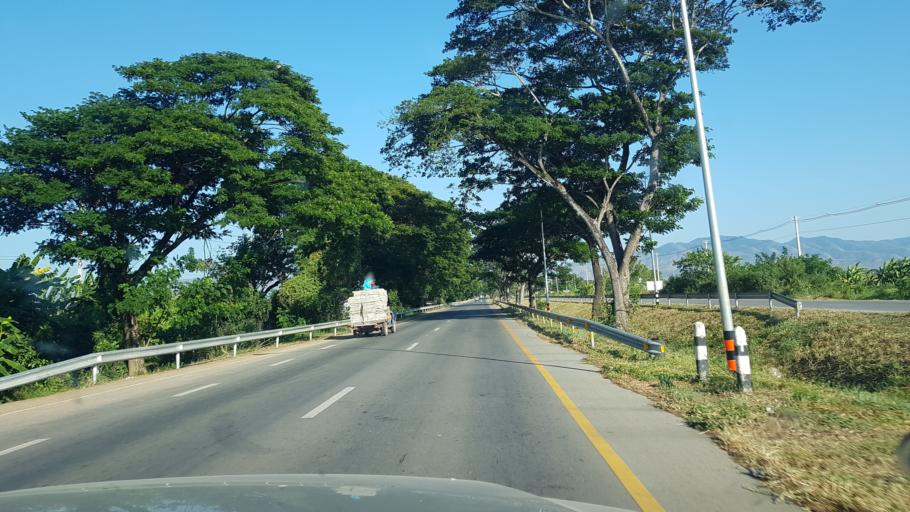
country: TH
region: Phetchabun
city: Lom Sak
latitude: 16.7273
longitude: 101.2621
